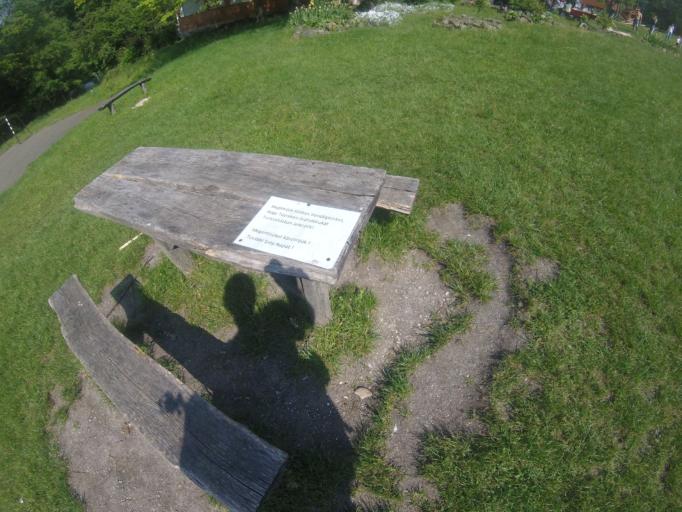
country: HU
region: Pest
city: Nagymaros
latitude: 47.8309
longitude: 18.9426
